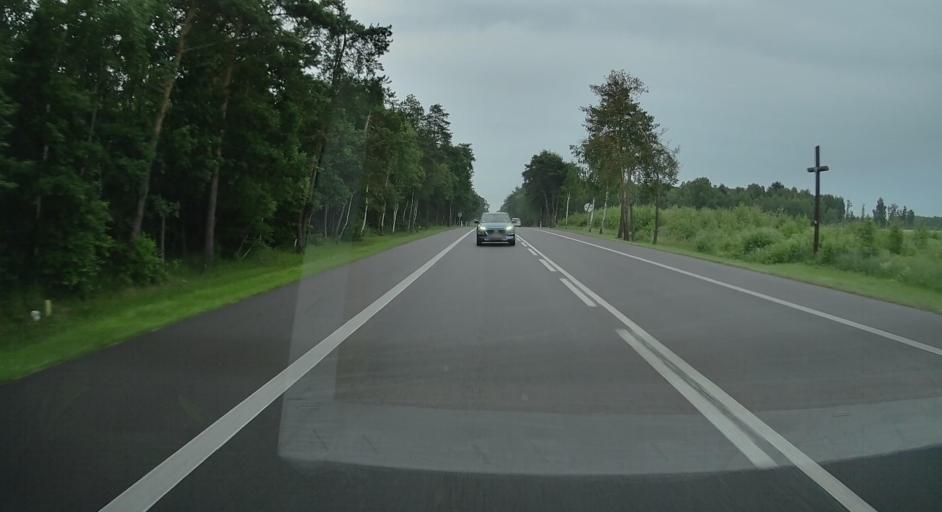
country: PL
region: Lublin Voivodeship
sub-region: Powiat bialski
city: Miedzyrzec Podlaski
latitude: 52.0107
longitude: 22.8351
